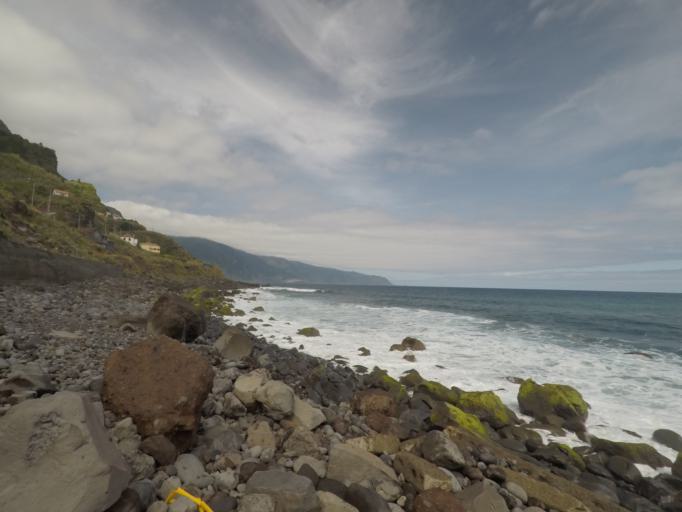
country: PT
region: Madeira
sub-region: Sao Vicente
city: Sao Vicente
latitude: 32.8211
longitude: -17.0003
